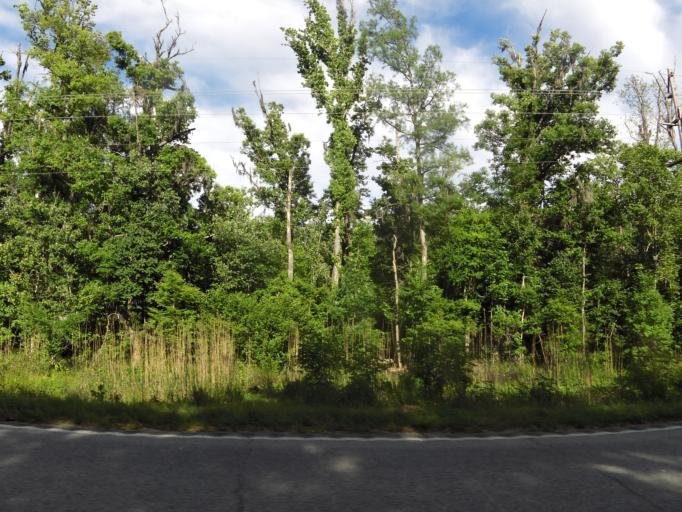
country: US
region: South Carolina
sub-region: Allendale County
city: Fairfax
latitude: 32.9086
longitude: -81.2377
